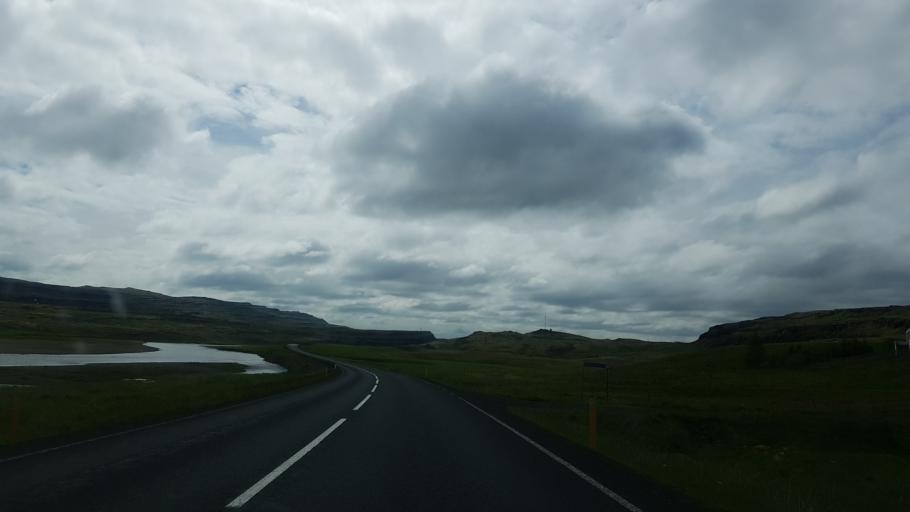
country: IS
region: West
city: Borgarnes
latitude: 64.8148
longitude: -21.4109
